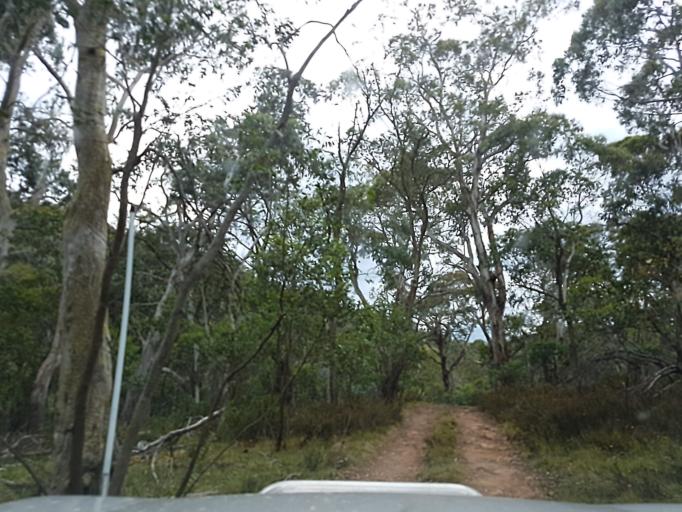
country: AU
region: New South Wales
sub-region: Snowy River
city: Jindabyne
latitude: -36.8868
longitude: 148.1284
